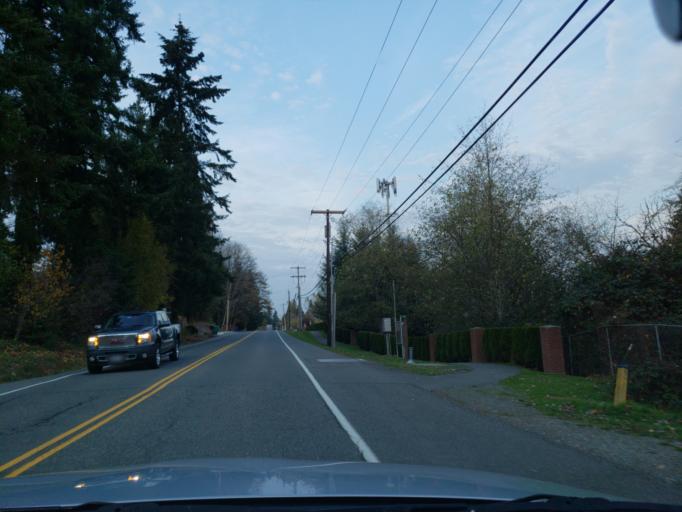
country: US
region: Washington
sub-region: King County
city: Kingsgate
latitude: 47.7425
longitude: -122.1916
